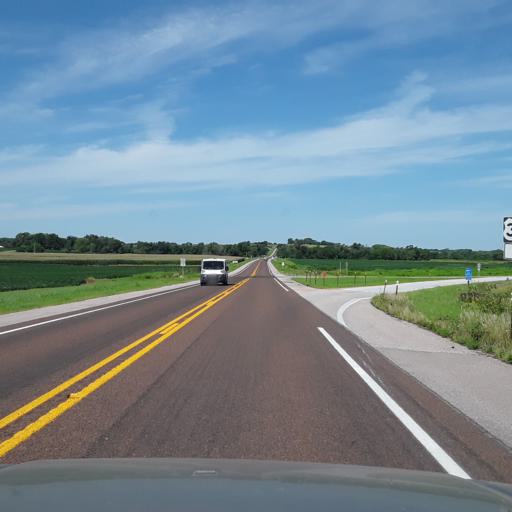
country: US
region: Nebraska
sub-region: Lancaster County
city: Lincoln
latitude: 40.8865
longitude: -96.8262
